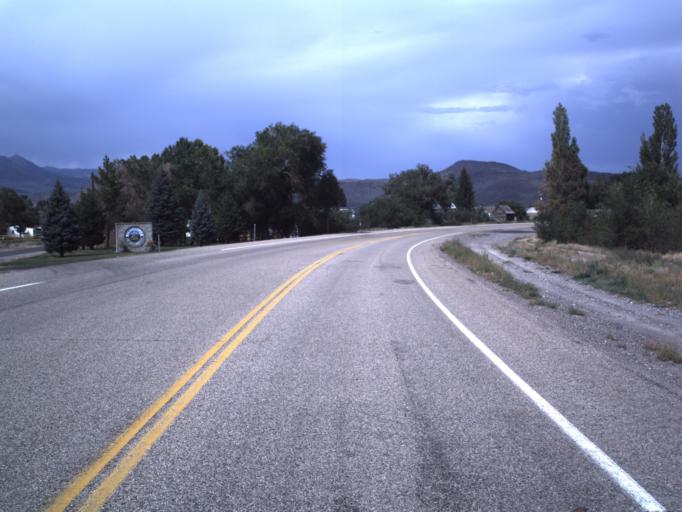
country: US
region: Utah
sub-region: Piute County
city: Junction
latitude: 38.1691
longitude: -112.2795
